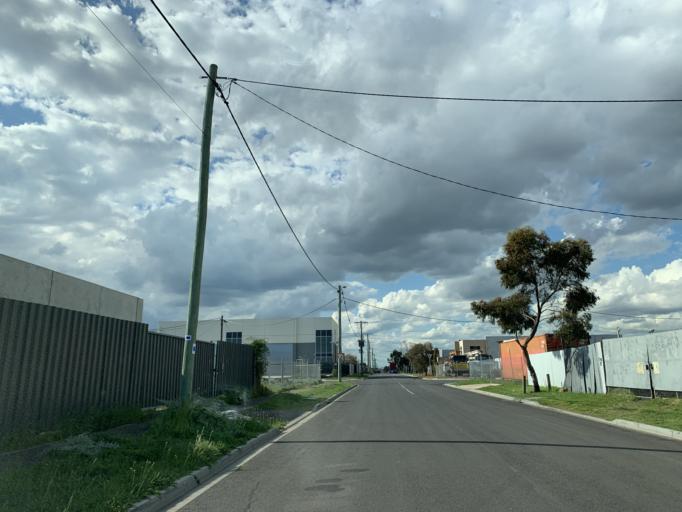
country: AU
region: Victoria
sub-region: Brimbank
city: Albion
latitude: -37.7539
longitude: 144.8382
